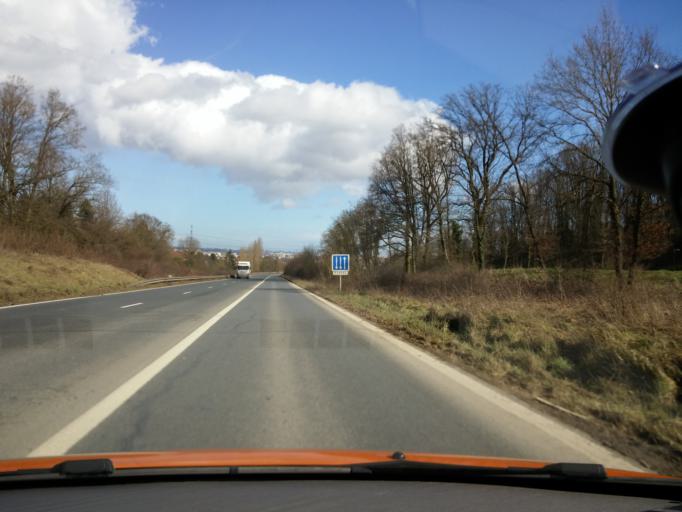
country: FR
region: Ile-de-France
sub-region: Departement de l'Essonne
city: Palaiseau
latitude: 48.7225
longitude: 2.2340
